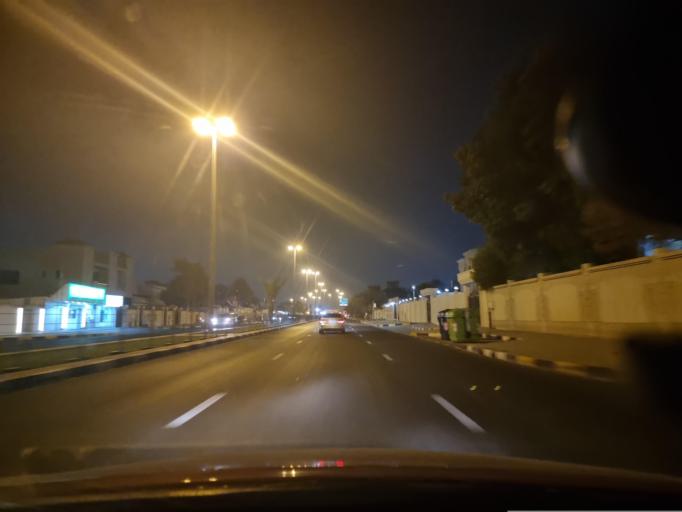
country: AE
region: Ash Shariqah
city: Sharjah
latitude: 25.3623
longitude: 55.4373
